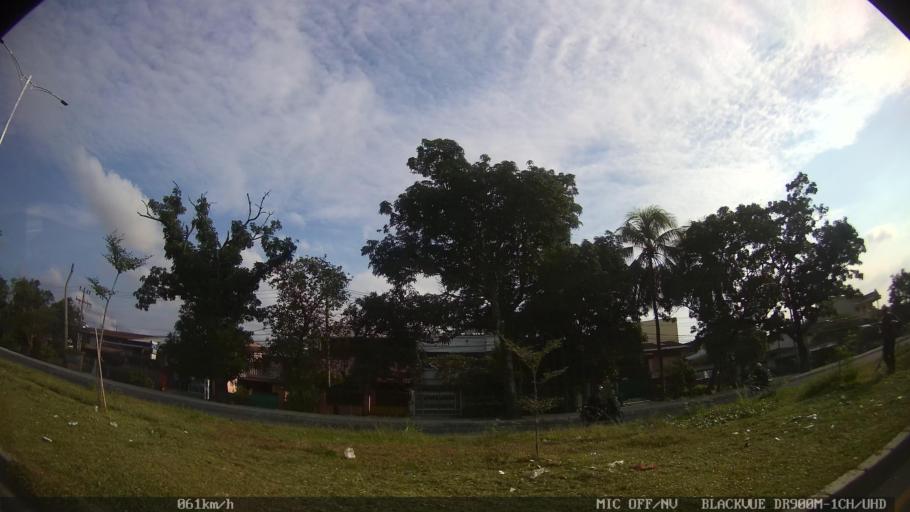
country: ID
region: North Sumatra
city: Medan
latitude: 3.6157
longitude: 98.6382
